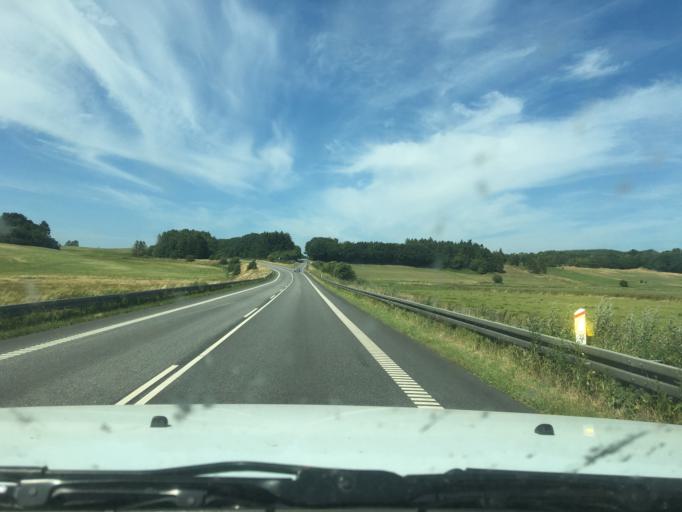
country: DK
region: Central Jutland
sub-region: Viborg Kommune
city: Viborg
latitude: 56.5416
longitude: 9.4024
